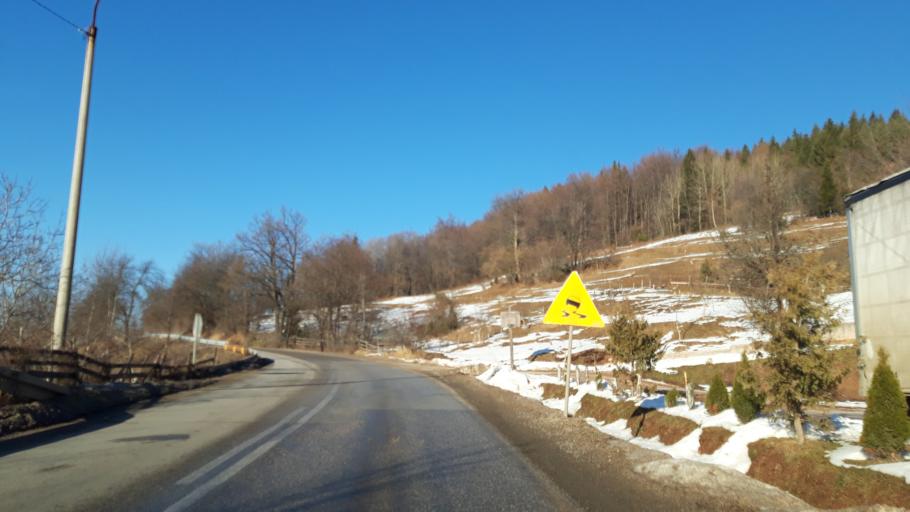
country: BA
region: Republika Srpska
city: Pale
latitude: 43.8960
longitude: 18.6362
